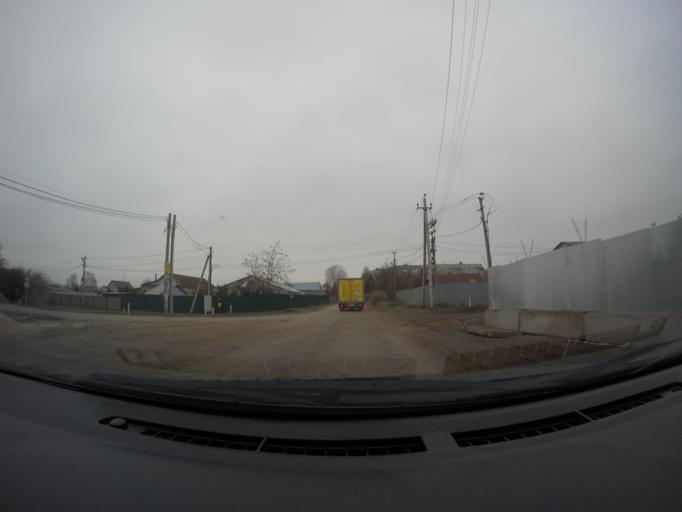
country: RU
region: Moskovskaya
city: Rechitsy
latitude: 55.5838
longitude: 38.5070
